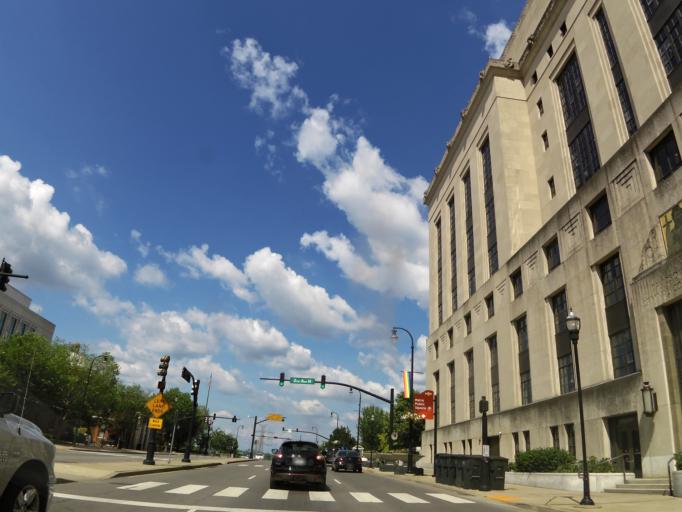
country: US
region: Tennessee
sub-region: Davidson County
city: Nashville
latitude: 36.1674
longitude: -86.7789
